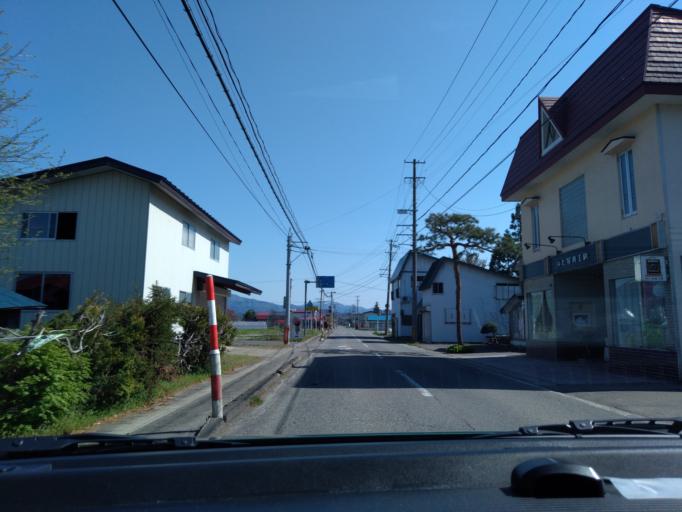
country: JP
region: Akita
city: Kakunodatemachi
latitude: 39.5229
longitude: 140.5879
